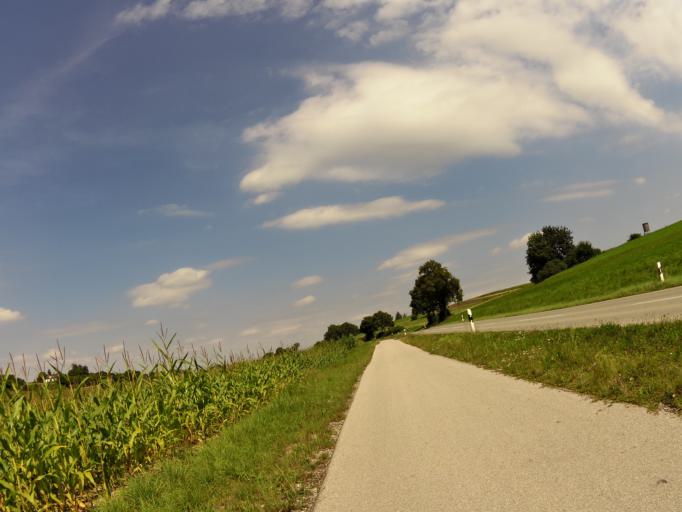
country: DE
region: Bavaria
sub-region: Upper Bavaria
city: Inning am Ammersee
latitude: 48.0632
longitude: 11.1436
